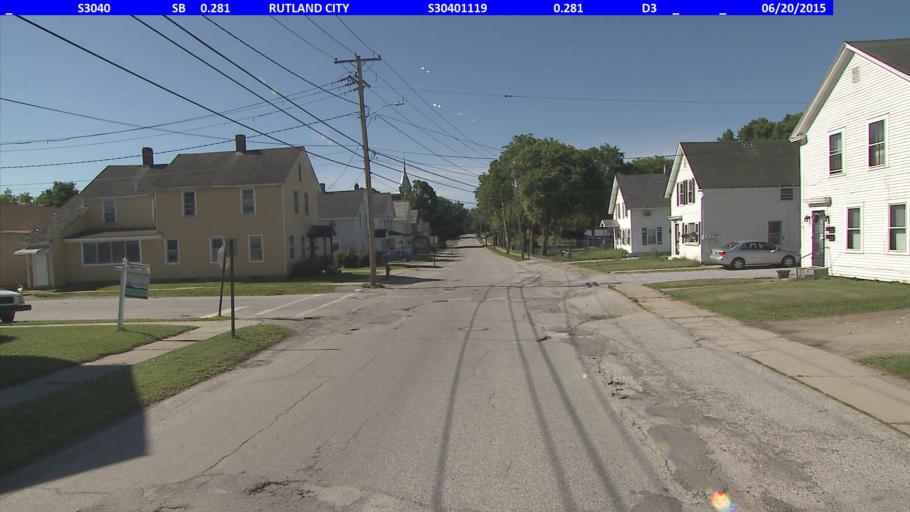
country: US
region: Vermont
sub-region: Rutland County
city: Rutland
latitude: 43.6052
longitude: -72.9868
